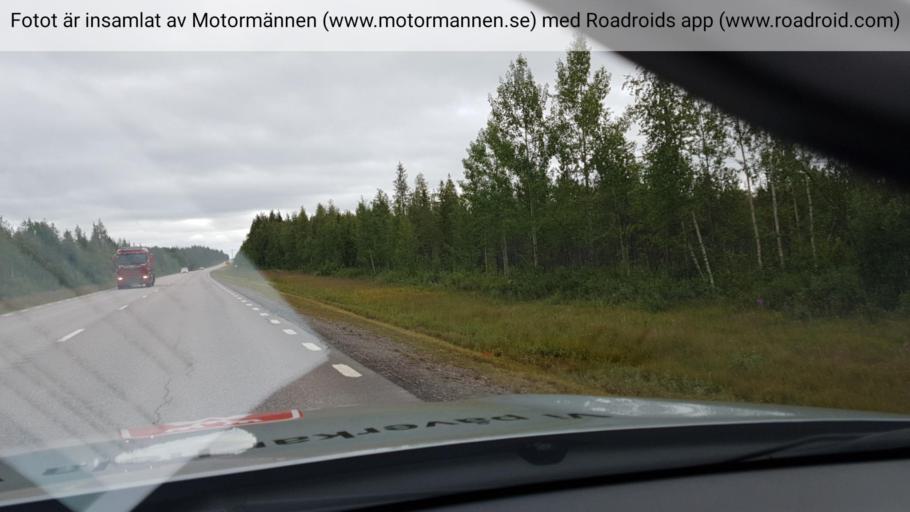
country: SE
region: Norrbotten
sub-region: Gallivare Kommun
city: Gaellivare
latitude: 67.0878
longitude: 21.0178
